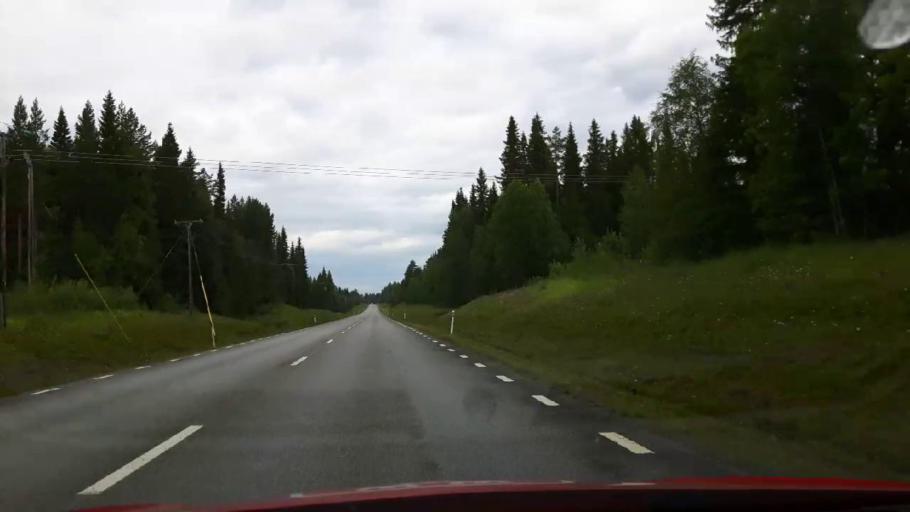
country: SE
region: Jaemtland
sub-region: Stroemsunds Kommun
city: Stroemsund
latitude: 63.6211
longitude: 15.3556
